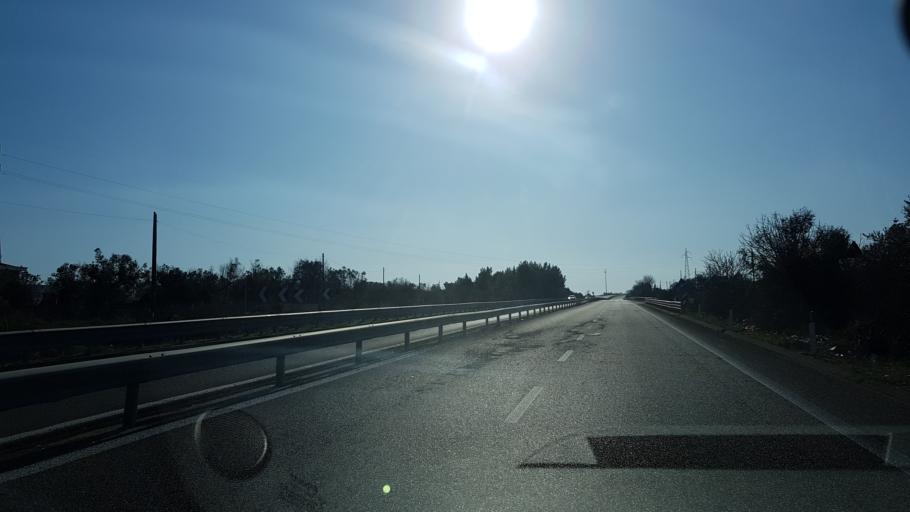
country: IT
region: Apulia
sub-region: Provincia di Lecce
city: Galatone
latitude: 40.1352
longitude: 18.0516
